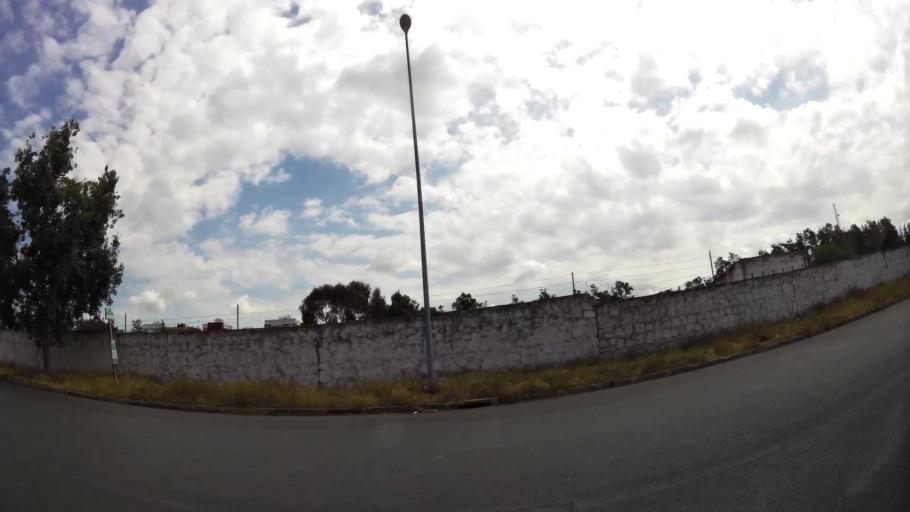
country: MA
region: Gharb-Chrarda-Beni Hssen
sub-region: Kenitra Province
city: Kenitra
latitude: 34.2506
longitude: -6.5944
